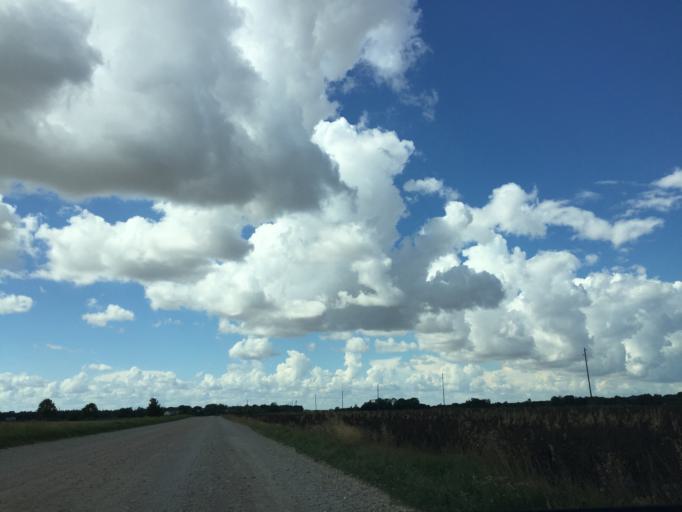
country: LV
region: Rundales
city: Pilsrundale
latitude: 56.3641
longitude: 24.0355
